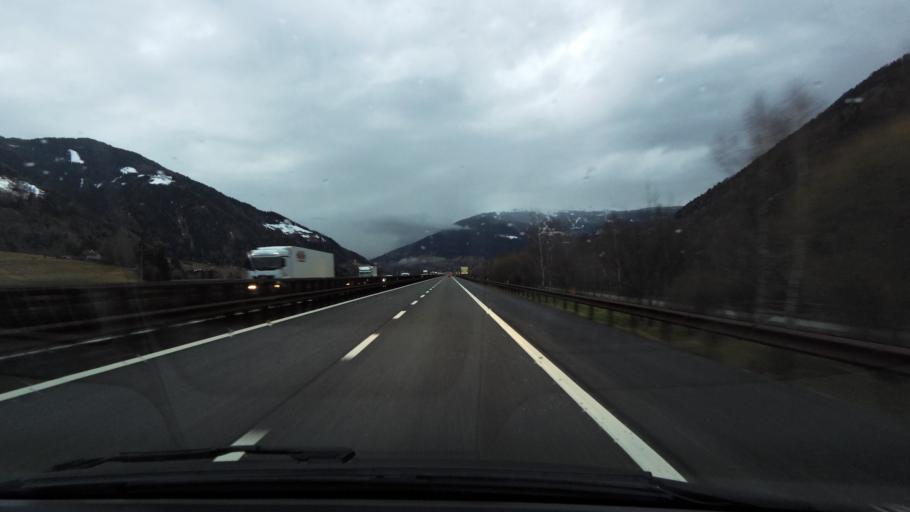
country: IT
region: Trentino-Alto Adige
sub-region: Bolzano
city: Campo di Trens
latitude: 46.8730
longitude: 11.4702
